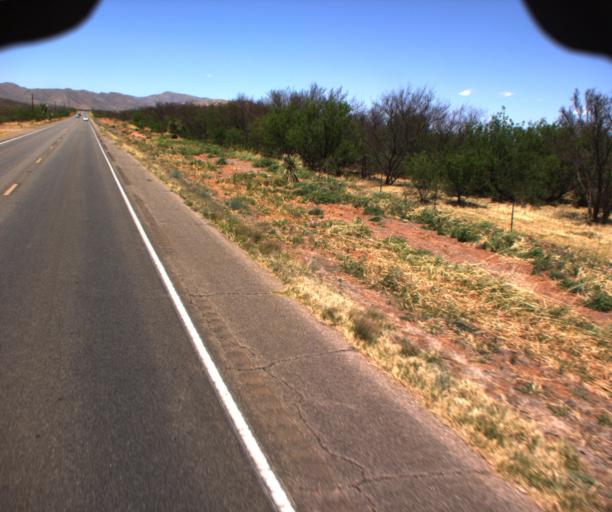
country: US
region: Arizona
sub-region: Cochise County
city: Pirtleville
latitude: 31.3804
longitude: -109.7481
